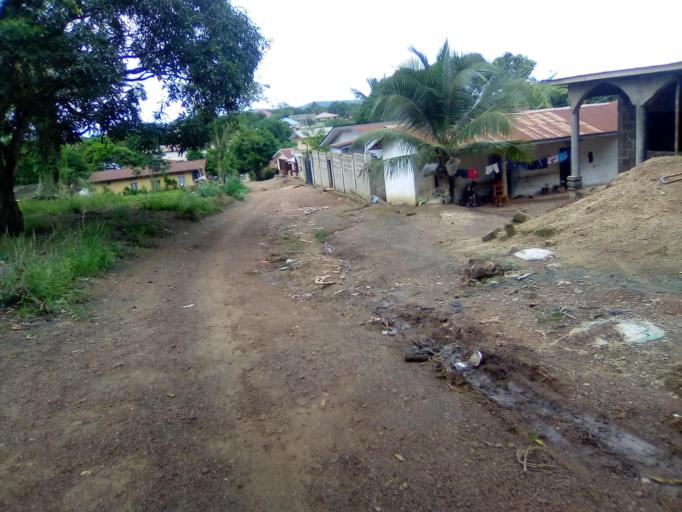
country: SL
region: Southern Province
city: Bo
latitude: 7.9449
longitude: -11.7182
